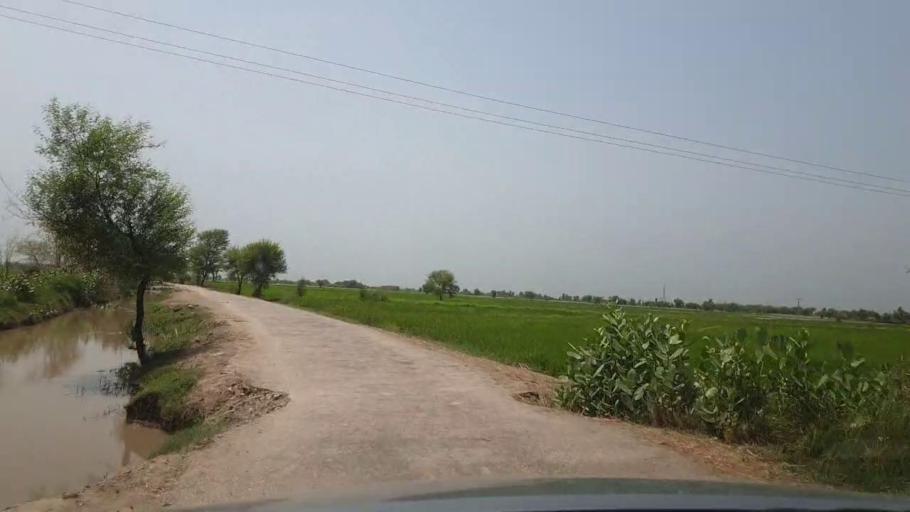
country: PK
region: Sindh
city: Madeji
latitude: 27.7815
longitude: 68.4324
